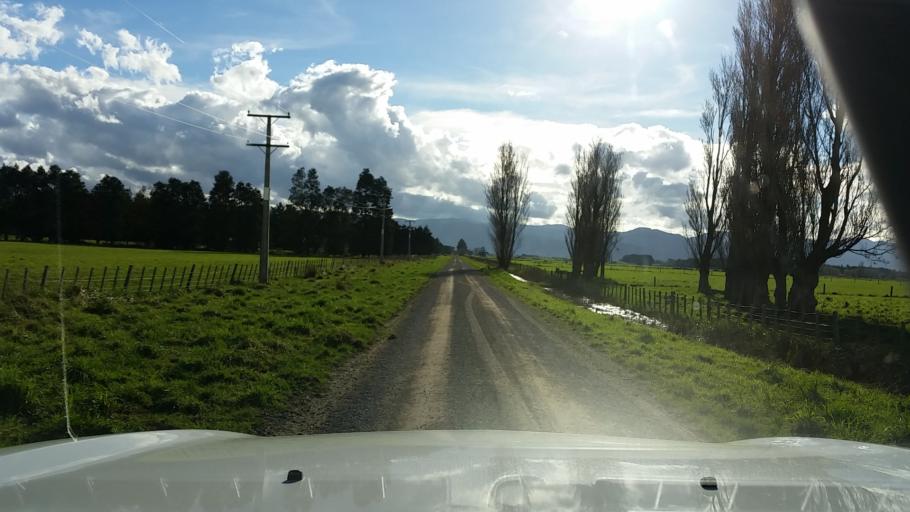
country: NZ
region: Wellington
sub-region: South Wairarapa District
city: Waipawa
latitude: -41.2449
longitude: 175.3100
